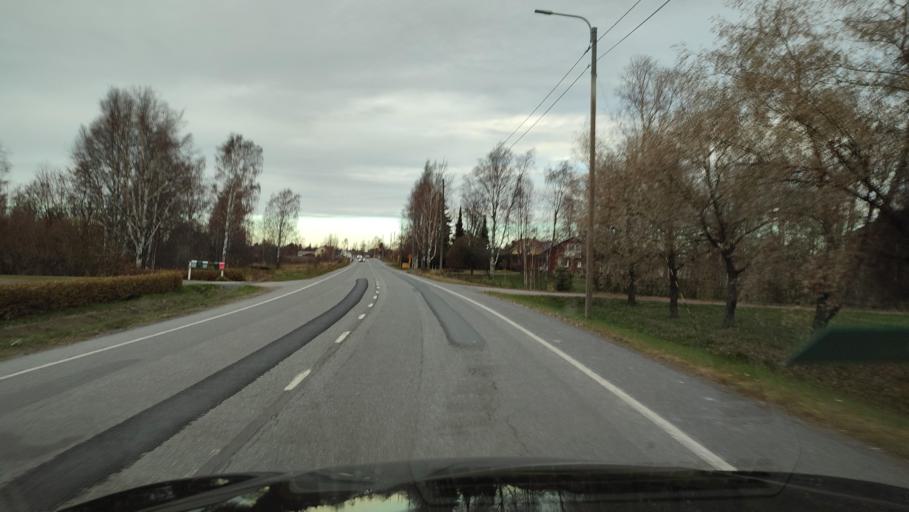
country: FI
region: Ostrobothnia
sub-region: Sydosterbotten
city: Naerpes
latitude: 62.4619
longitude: 21.3565
